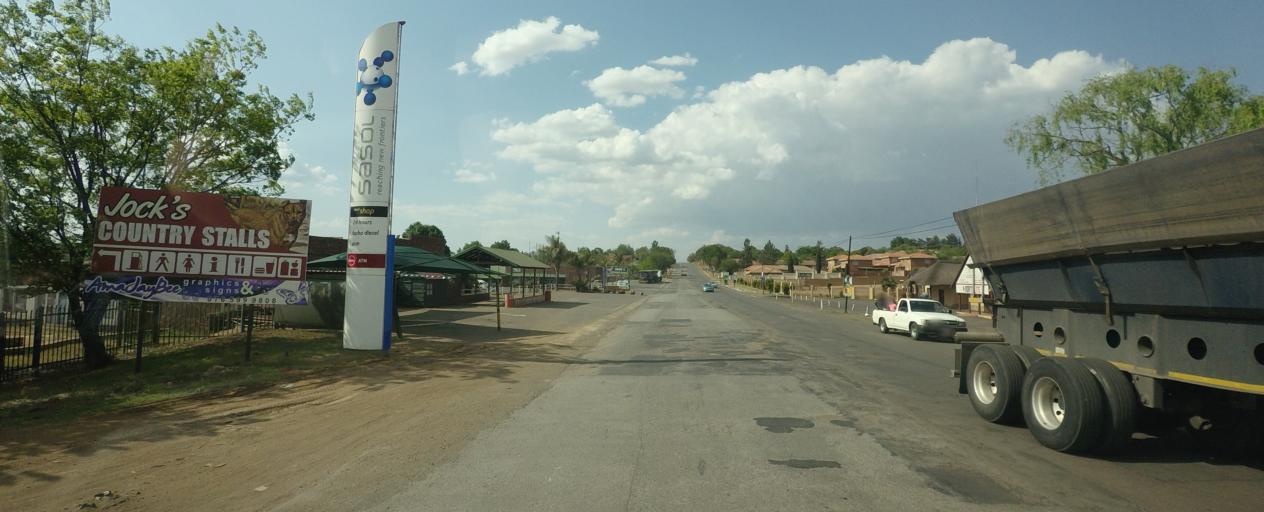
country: ZA
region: Mpumalanga
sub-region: Ehlanzeni District
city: Lydenburg
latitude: -25.1126
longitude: 30.4477
